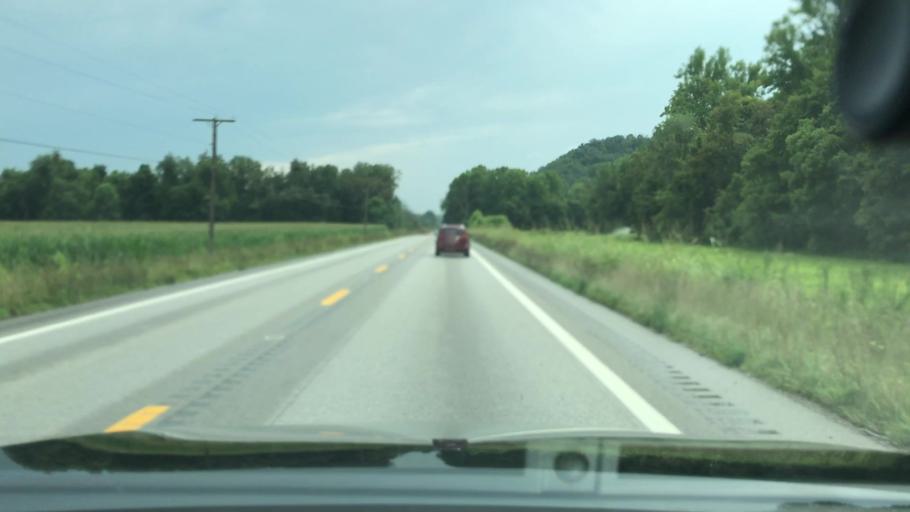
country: US
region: West Virginia
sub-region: Putnam County
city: Buffalo
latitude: 38.6274
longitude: -81.9821
